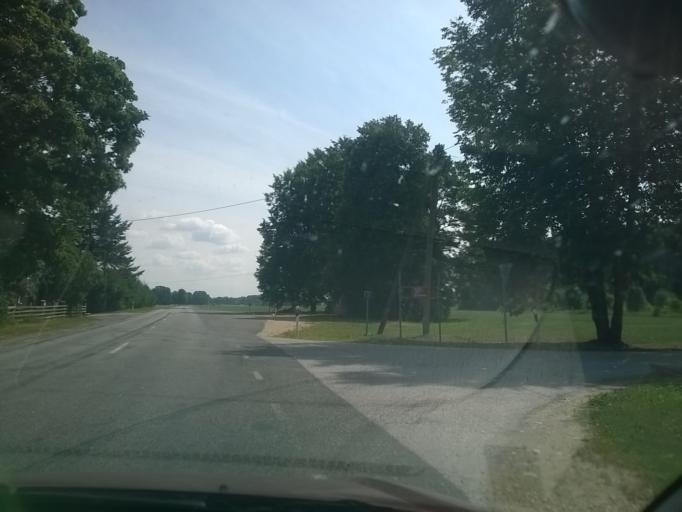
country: EE
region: Tartu
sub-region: Puhja vald
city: Puhja
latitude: 58.2536
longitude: 26.1819
